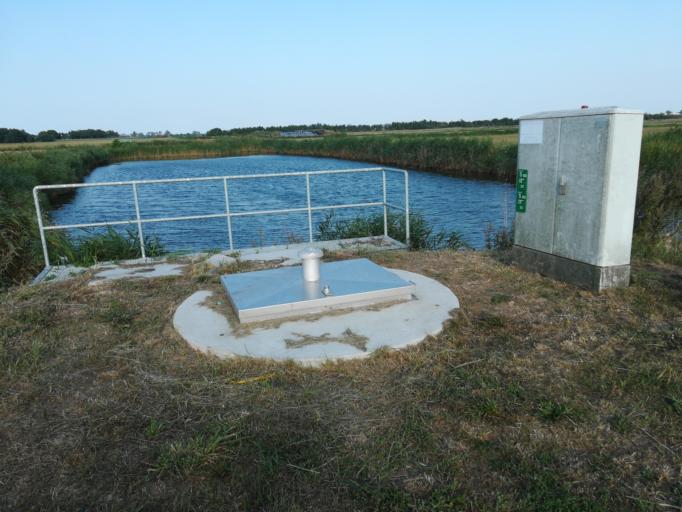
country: DE
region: Mecklenburg-Vorpommern
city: Zingst
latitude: 54.4158
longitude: 12.6489
